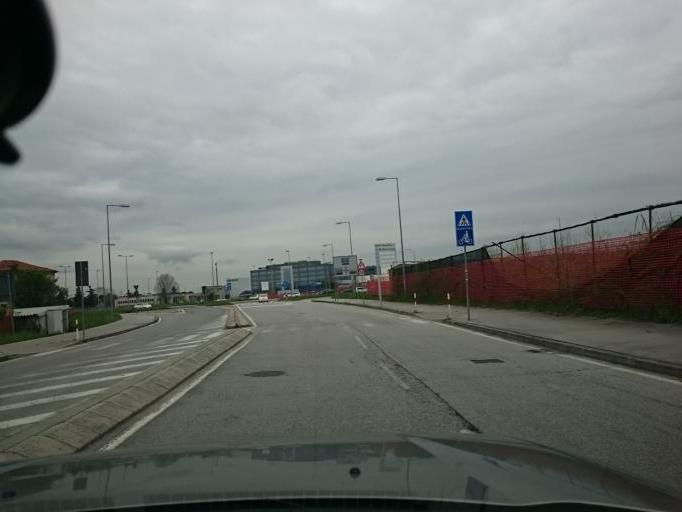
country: IT
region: Veneto
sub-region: Provincia di Padova
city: Cadoneghe
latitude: 45.4174
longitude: 11.9213
